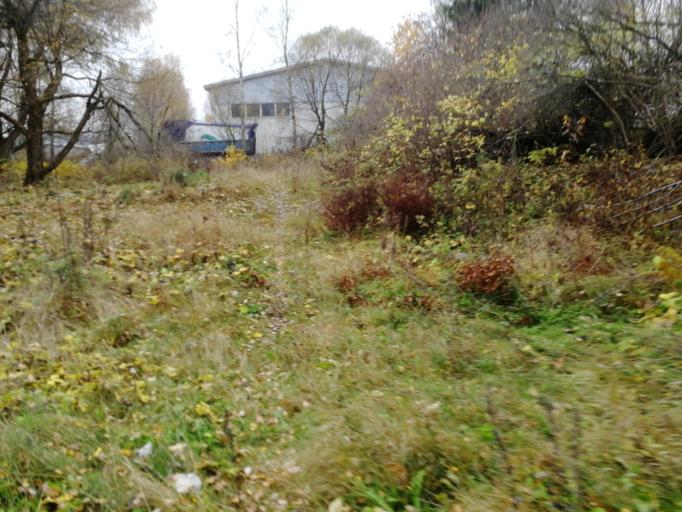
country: FI
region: Pirkanmaa
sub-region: Tampere
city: Tampere
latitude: 61.4489
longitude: 23.8984
